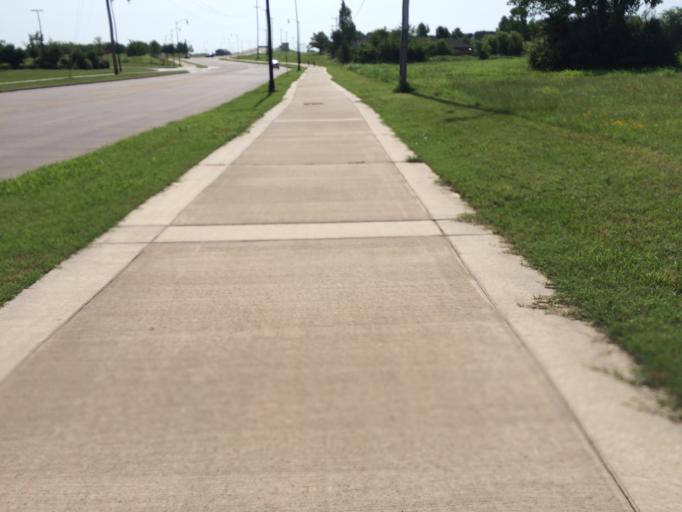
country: US
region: Oklahoma
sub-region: Cleveland County
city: Norman
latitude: 35.2473
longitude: -97.4938
